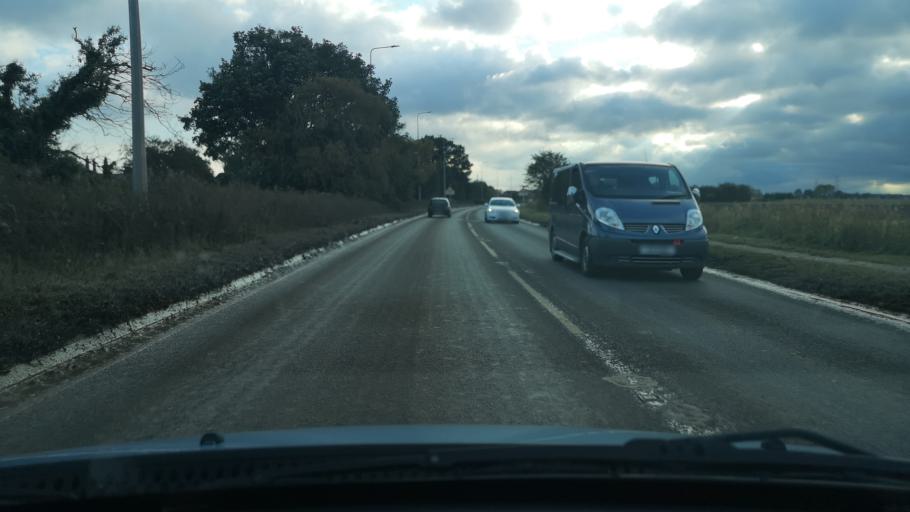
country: GB
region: England
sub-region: North Lincolnshire
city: Gunness
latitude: 53.5813
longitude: -0.7390
